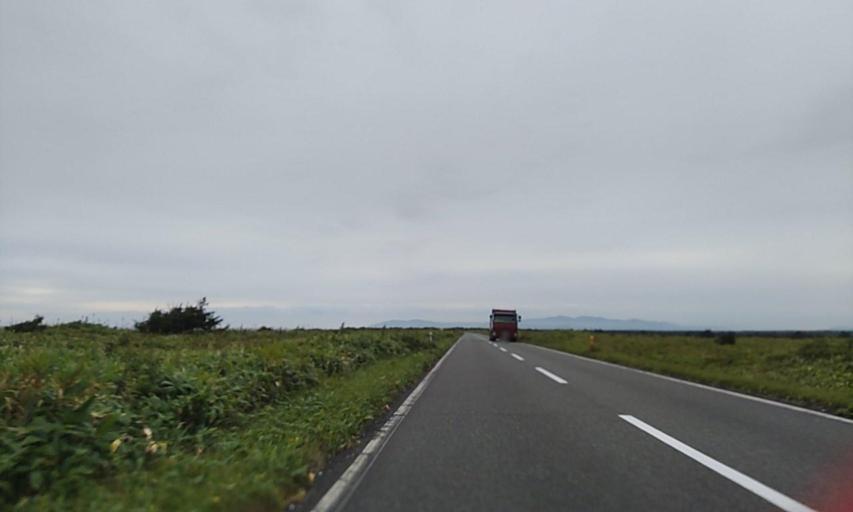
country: JP
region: Hokkaido
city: Makubetsu
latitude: 45.2604
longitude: 142.2462
